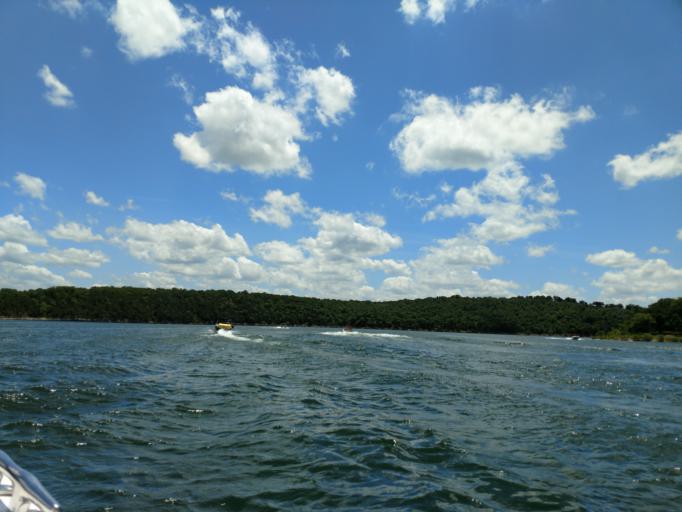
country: US
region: Missouri
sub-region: Barry County
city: Shell Knob
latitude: 36.5964
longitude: -93.5427
